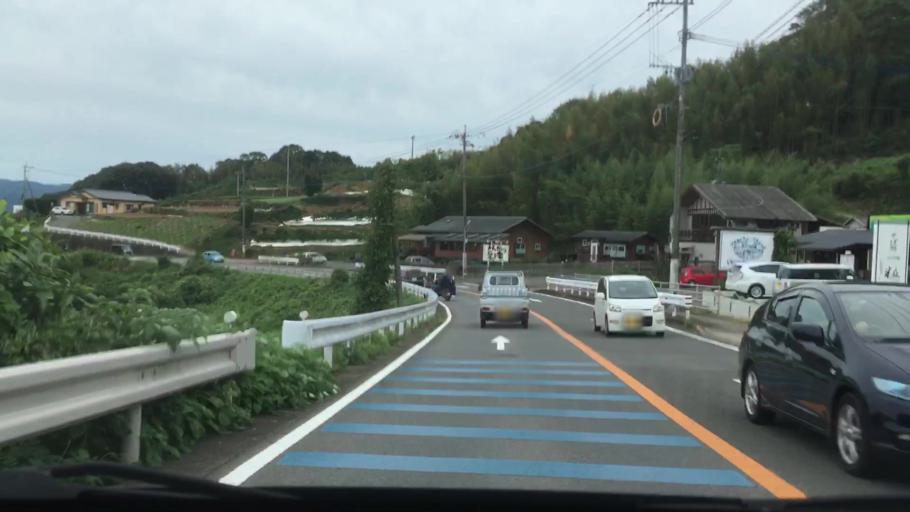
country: JP
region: Nagasaki
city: Sasebo
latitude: 33.0346
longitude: 129.7446
